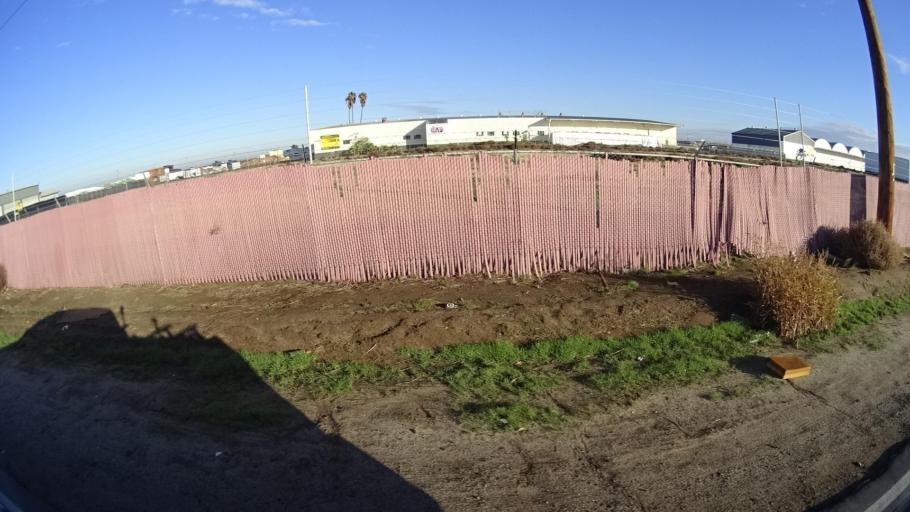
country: US
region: California
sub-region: Kern County
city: Delano
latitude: 35.7904
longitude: -119.2569
